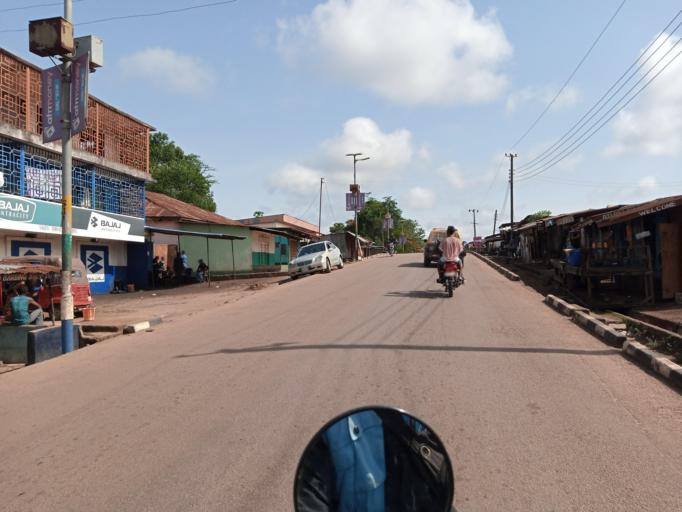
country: SL
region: Southern Province
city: Bo
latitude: 7.9614
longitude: -11.7338
